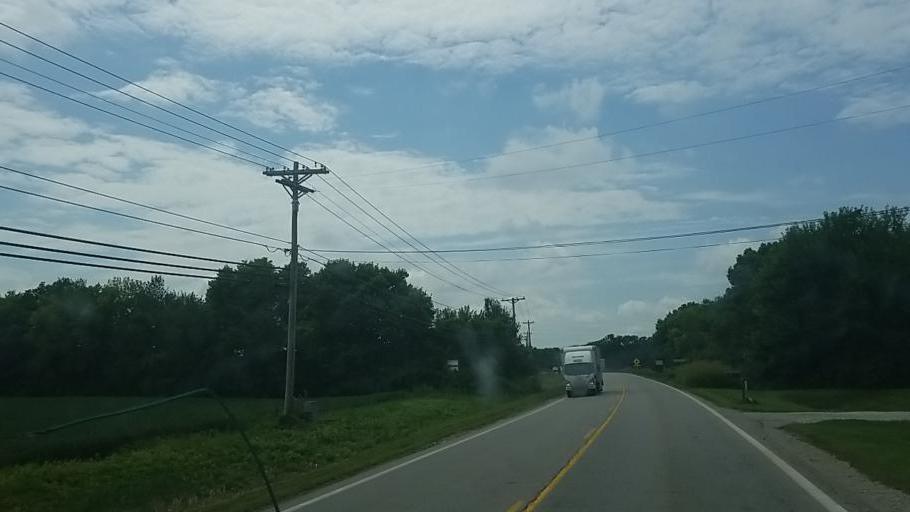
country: US
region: Ohio
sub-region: Franklin County
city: Obetz
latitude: 39.8317
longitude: -82.9699
